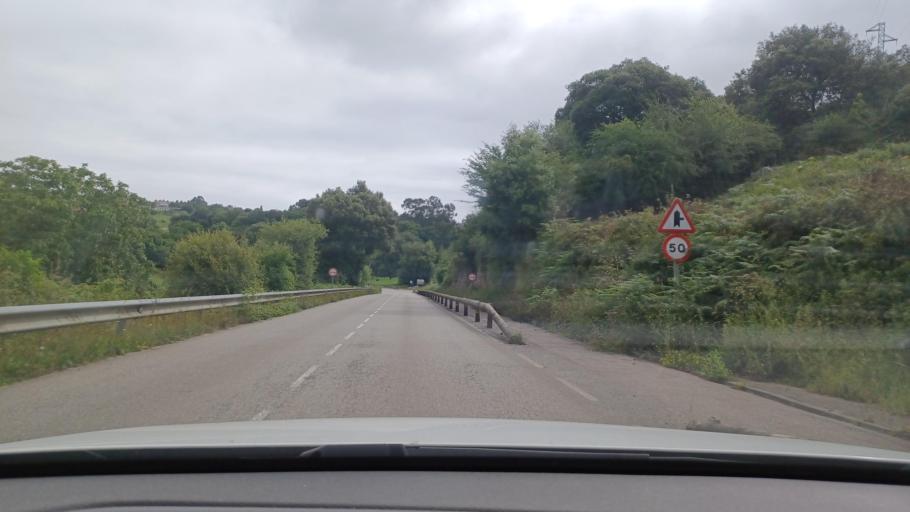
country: ES
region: Asturias
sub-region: Province of Asturias
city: Ribadesella
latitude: 43.4567
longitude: -5.0954
